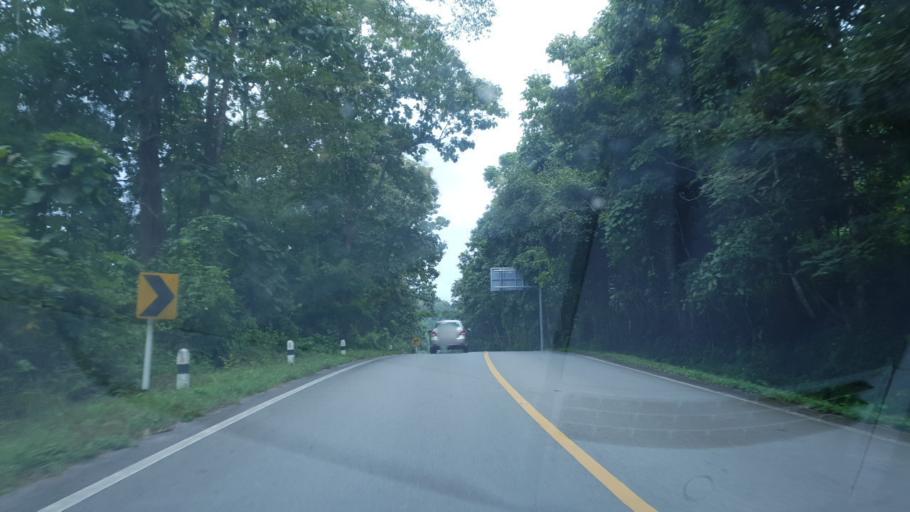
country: TH
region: Mae Hong Son
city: Khun Yuam
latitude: 18.7133
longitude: 97.9105
